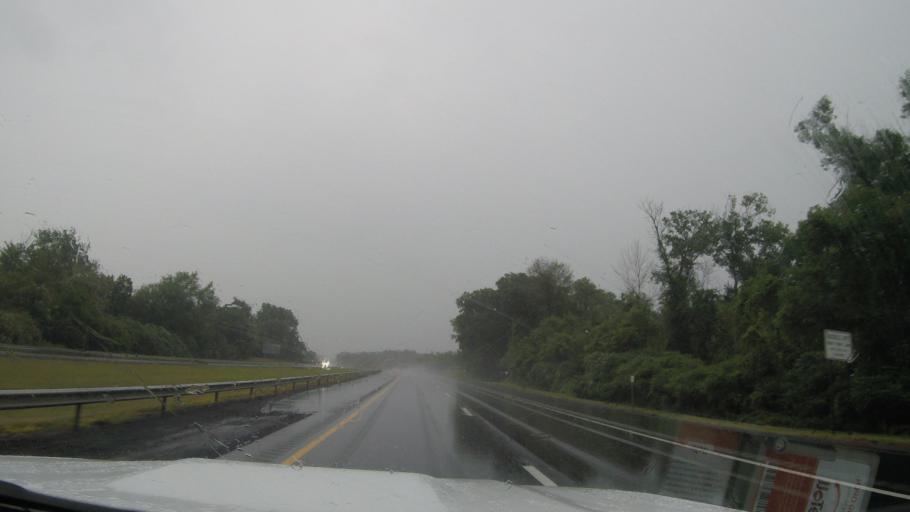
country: US
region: New York
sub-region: Ontario County
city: Geneva
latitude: 42.9551
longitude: -76.9664
